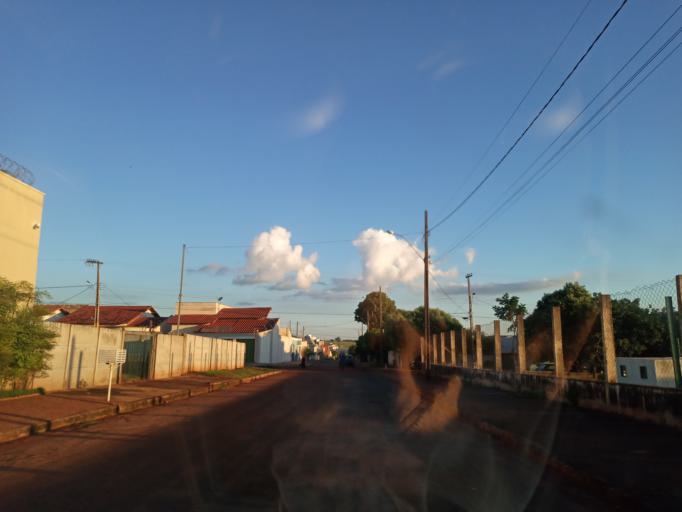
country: BR
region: Minas Gerais
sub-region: Ituiutaba
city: Ituiutaba
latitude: -18.9928
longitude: -49.4650
